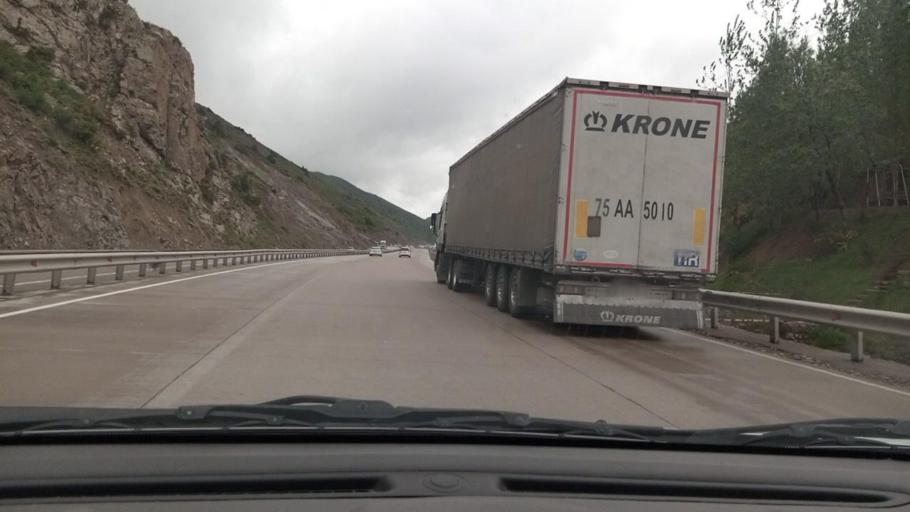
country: UZ
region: Toshkent
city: Angren
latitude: 41.0472
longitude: 70.5713
